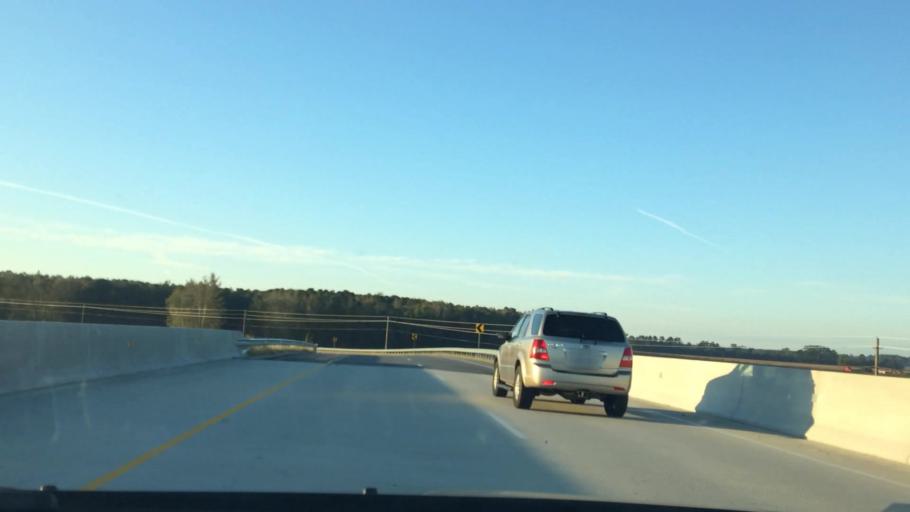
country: US
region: North Carolina
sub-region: Pitt County
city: Ayden
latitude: 35.4627
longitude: -77.4365
